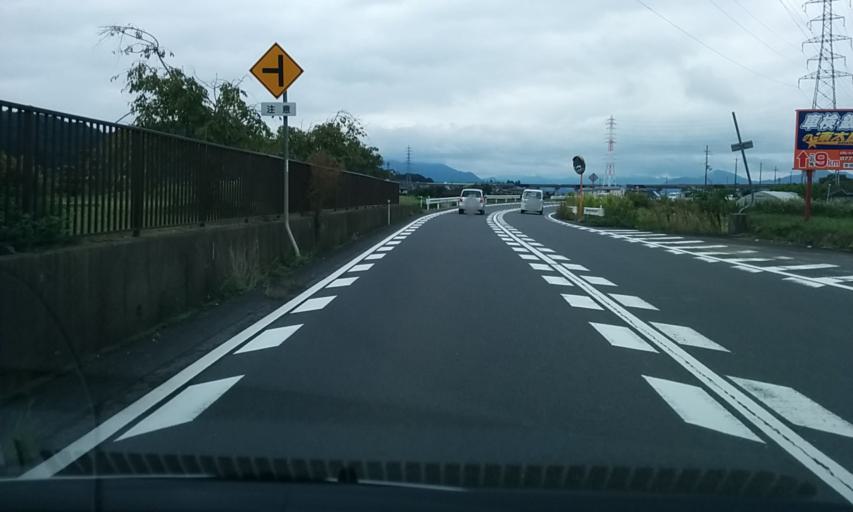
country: JP
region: Kyoto
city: Ayabe
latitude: 35.3064
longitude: 135.1986
